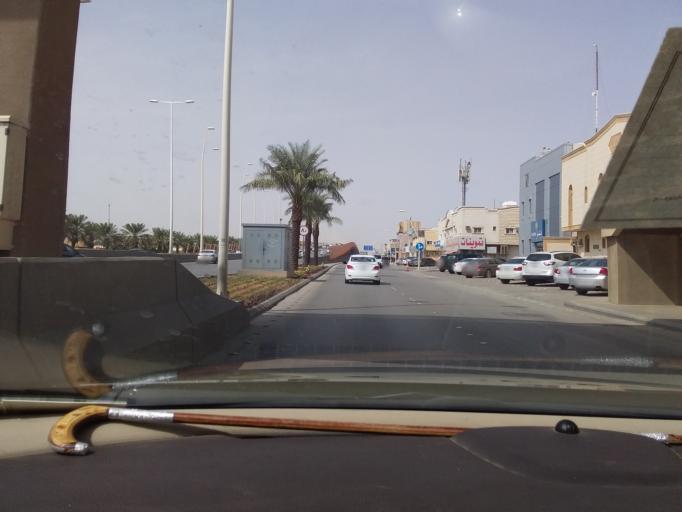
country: SA
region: Ar Riyad
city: Riyadh
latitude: 24.7398
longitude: 46.7056
